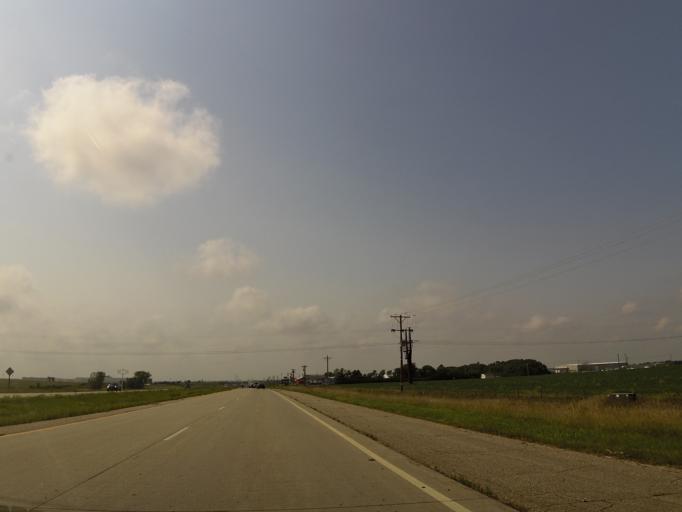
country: US
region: South Dakota
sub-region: Codington County
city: Watertown
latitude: 44.8901
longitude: -97.0414
